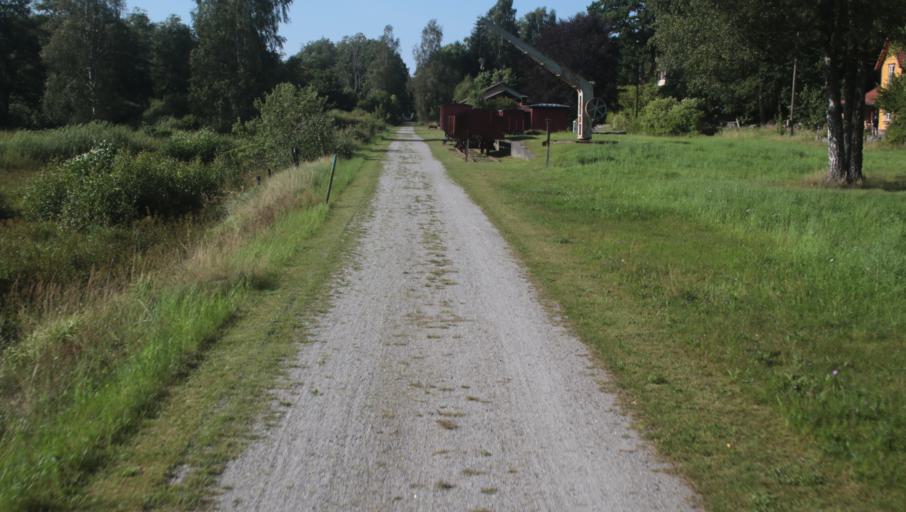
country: SE
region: Blekinge
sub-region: Karlshamns Kommun
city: Svangsta
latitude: 56.3503
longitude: 14.6943
